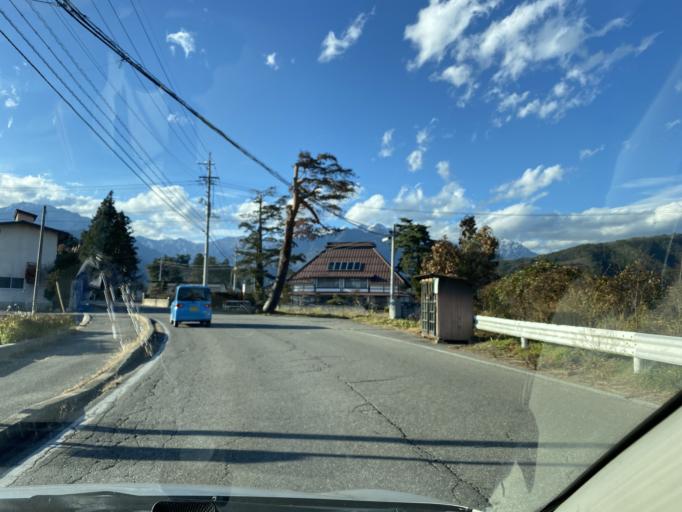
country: JP
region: Nagano
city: Omachi
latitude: 36.5209
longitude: 137.8370
